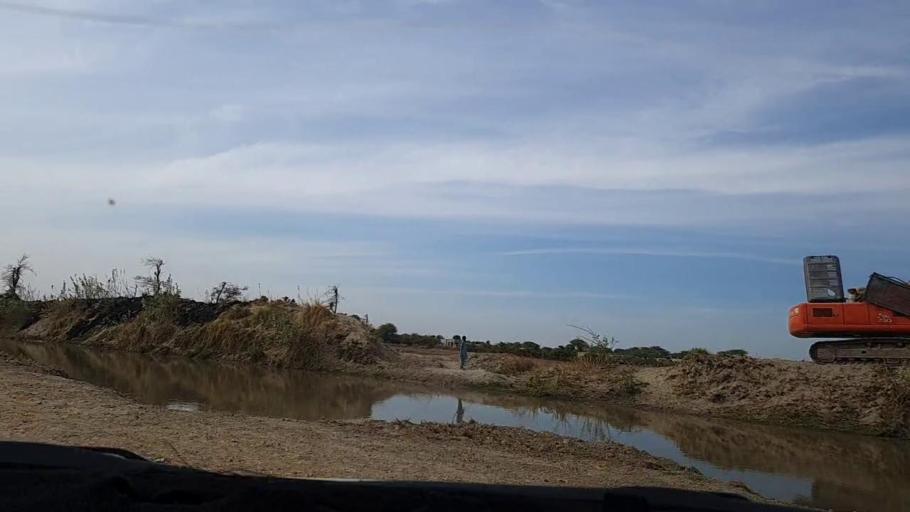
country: PK
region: Sindh
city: Dhoro Naro
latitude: 25.5185
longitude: 69.5236
